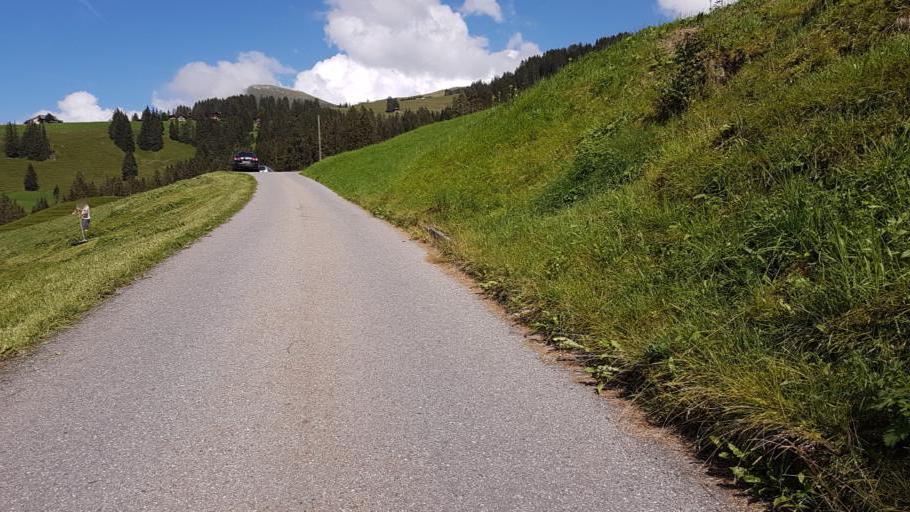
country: CH
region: Bern
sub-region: Frutigen-Niedersimmental District
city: Adelboden
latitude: 46.5100
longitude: 7.5958
